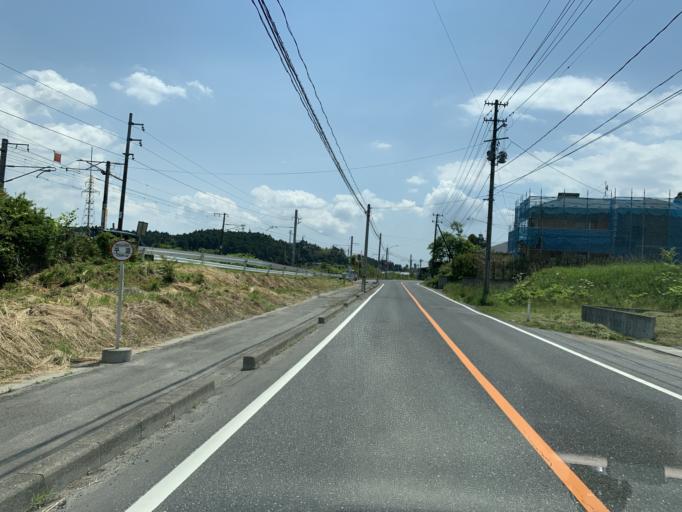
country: JP
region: Miyagi
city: Wakuya
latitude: 38.4856
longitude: 141.0959
